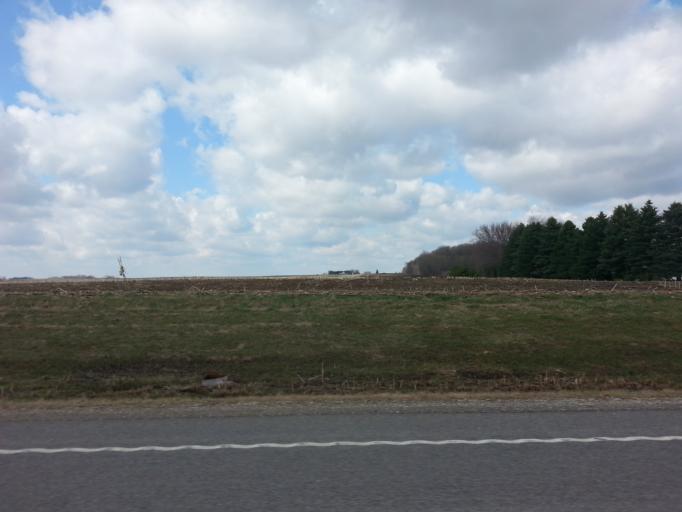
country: US
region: Minnesota
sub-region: Dodge County
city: Mantorville
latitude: 44.0798
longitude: -92.6962
